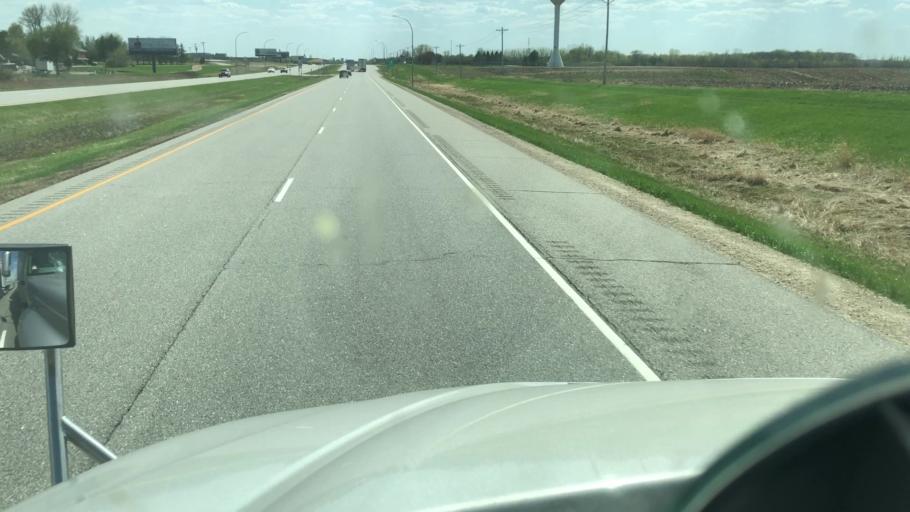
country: US
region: Minnesota
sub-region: Le Sueur County
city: Le Sueur
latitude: 44.5038
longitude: -93.8620
